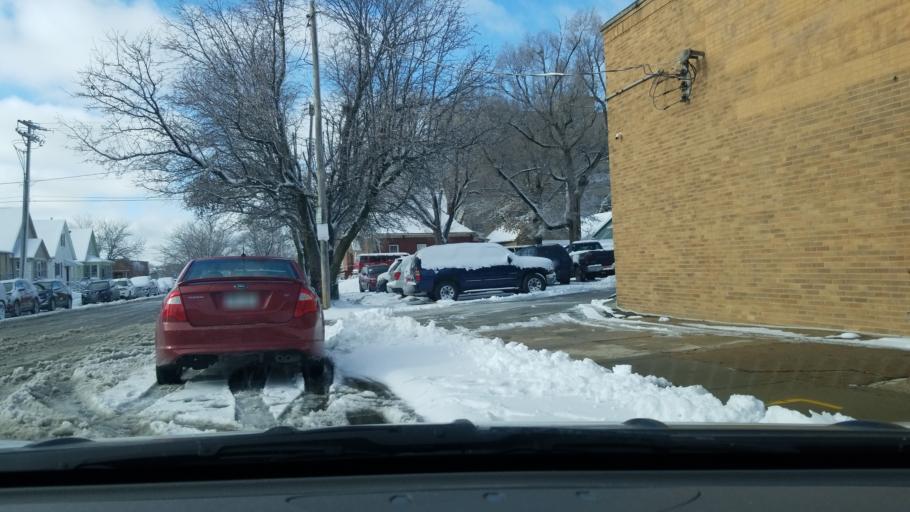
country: US
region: Nebraska
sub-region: Douglas County
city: Omaha
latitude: 41.2135
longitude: -95.9472
